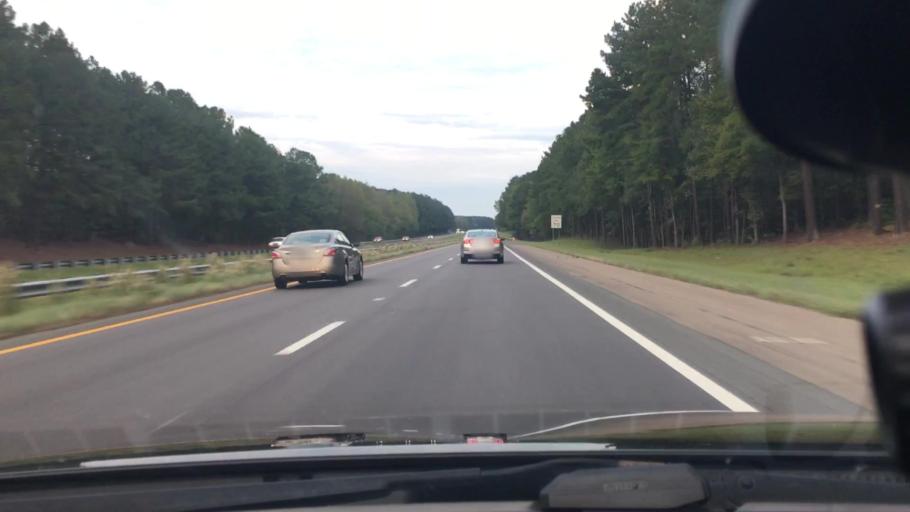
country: US
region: North Carolina
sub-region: Chatham County
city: Farmville
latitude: 35.5958
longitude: -79.1150
